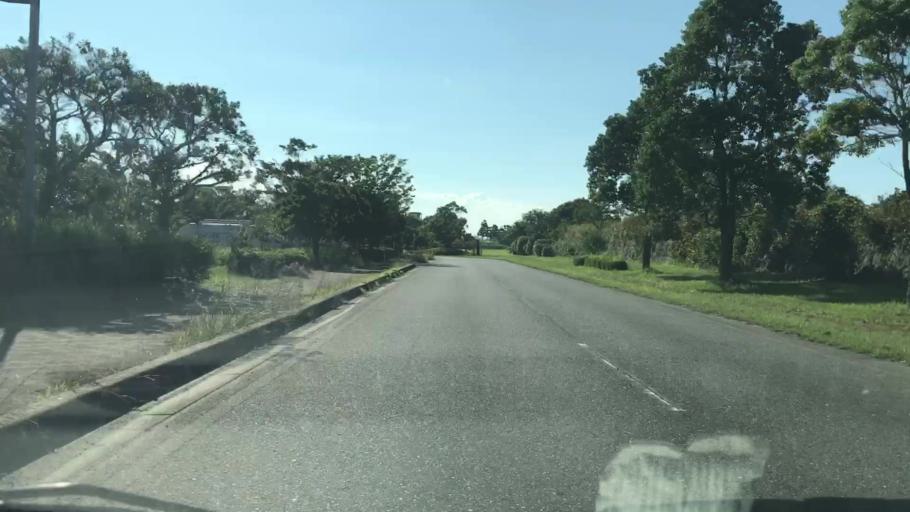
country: JP
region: Saga Prefecture
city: Okawa
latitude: 33.1527
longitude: 130.3097
